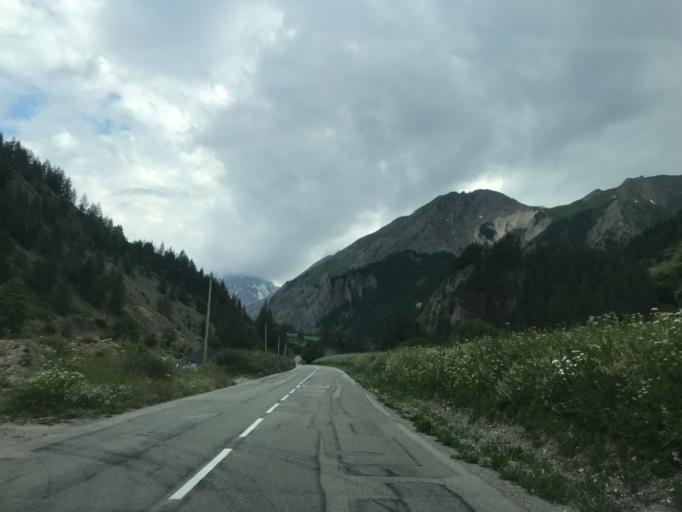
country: FR
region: Rhone-Alpes
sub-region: Departement de la Savoie
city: Valloire
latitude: 45.1298
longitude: 6.4184
